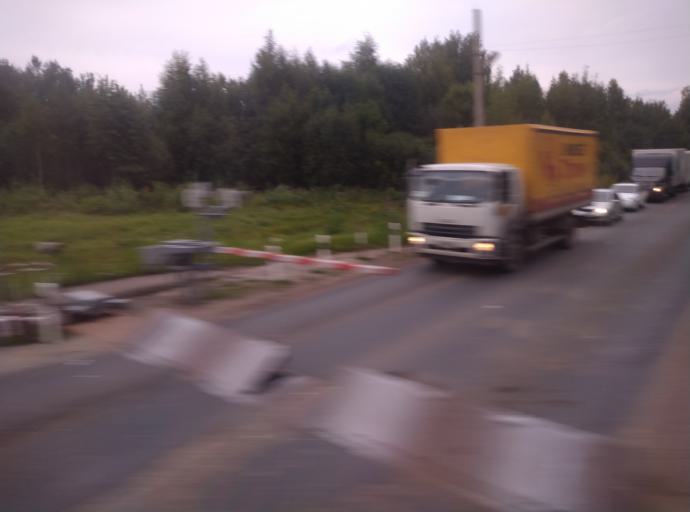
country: RU
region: Jaroslavl
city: Yaroslavl
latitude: 57.5434
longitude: 39.9370
